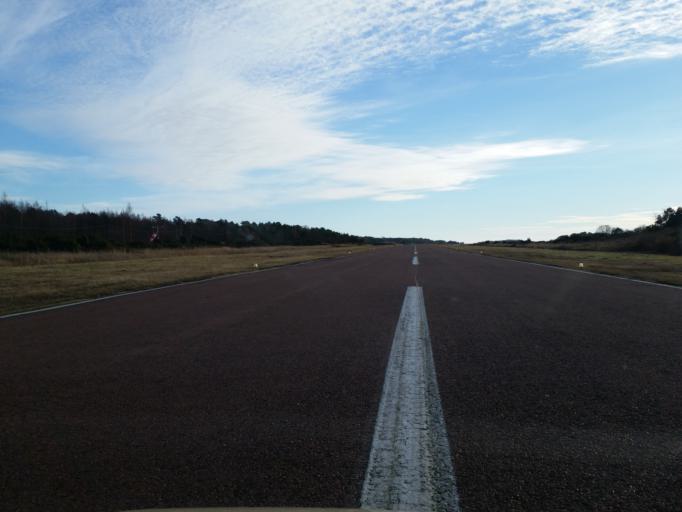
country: AX
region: Alands skaergard
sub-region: Kumlinge
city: Kumlinge
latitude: 60.2465
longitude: 20.8028
